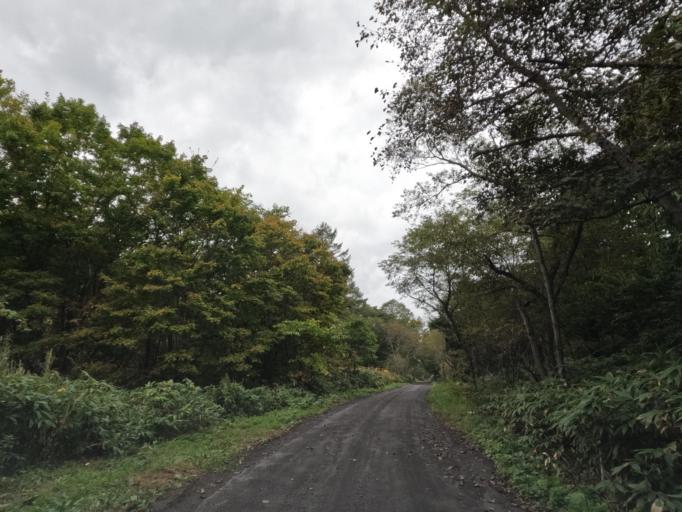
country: JP
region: Hokkaido
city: Date
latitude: 42.5017
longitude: 140.9183
